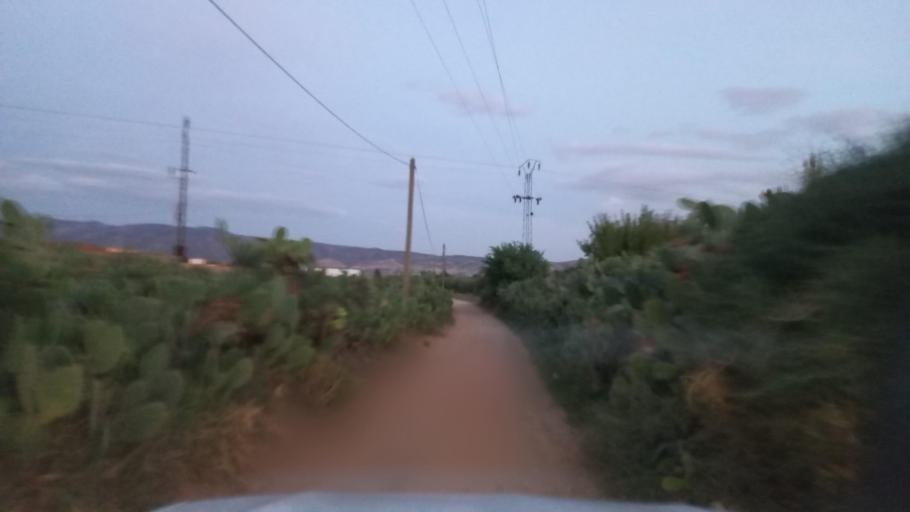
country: TN
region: Al Qasrayn
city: Sbiba
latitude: 35.4159
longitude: 9.1209
